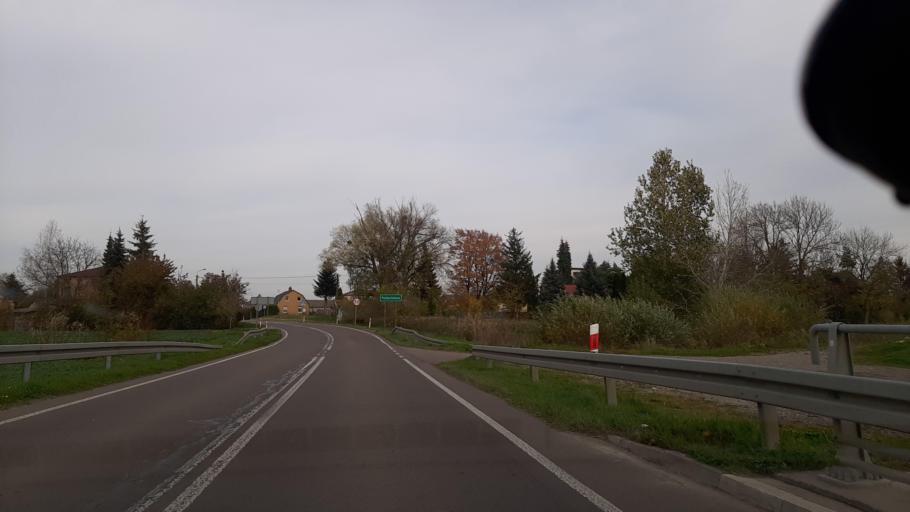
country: PL
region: Lublin Voivodeship
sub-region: Powiat pulawski
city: Markuszow
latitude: 51.3586
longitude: 22.2785
